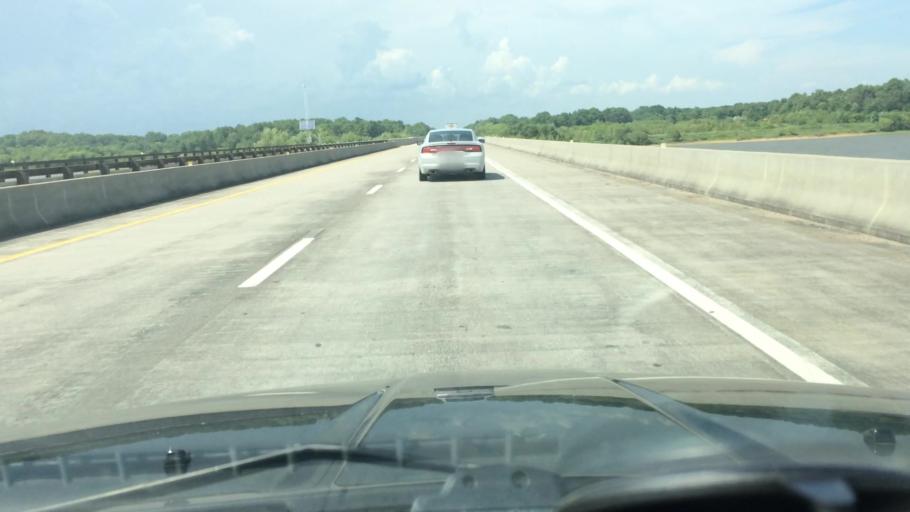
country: US
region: Missouri
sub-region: Henry County
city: Clinton
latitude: 38.2850
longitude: -93.7593
